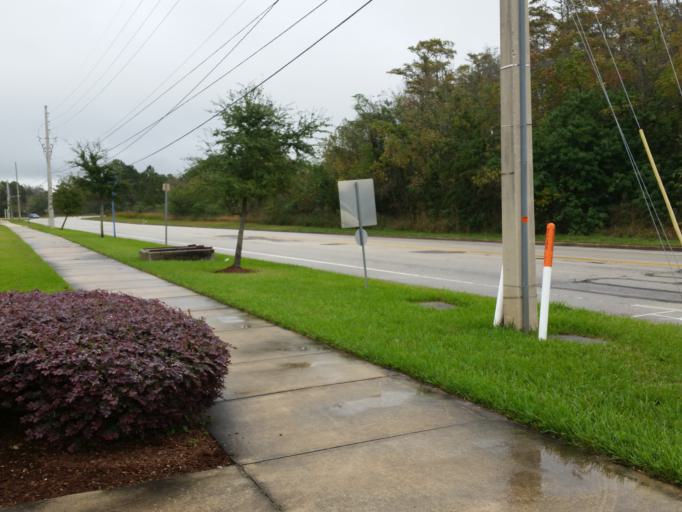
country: US
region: Florida
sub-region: Orange County
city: Tangelo Park
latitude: 28.4561
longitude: -81.4643
